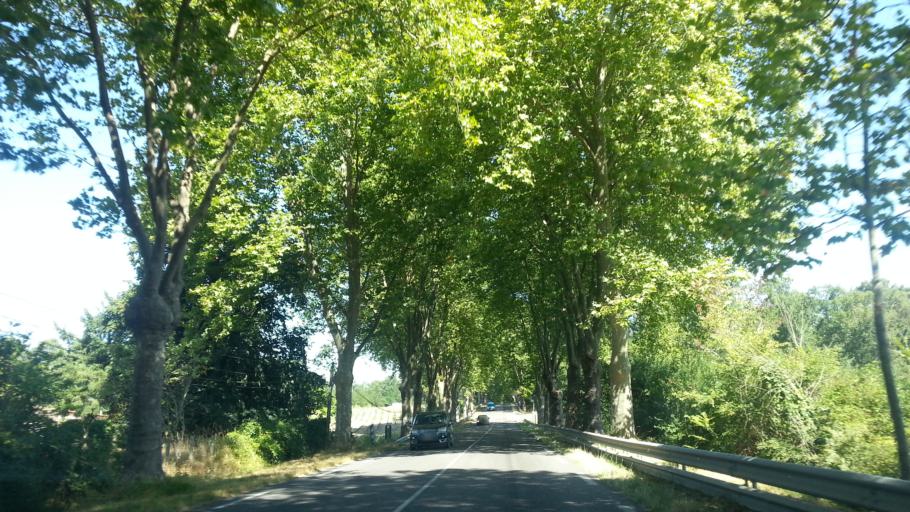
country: FR
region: Aquitaine
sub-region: Departement de la Gironde
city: Martillac
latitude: 44.7000
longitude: -0.5115
